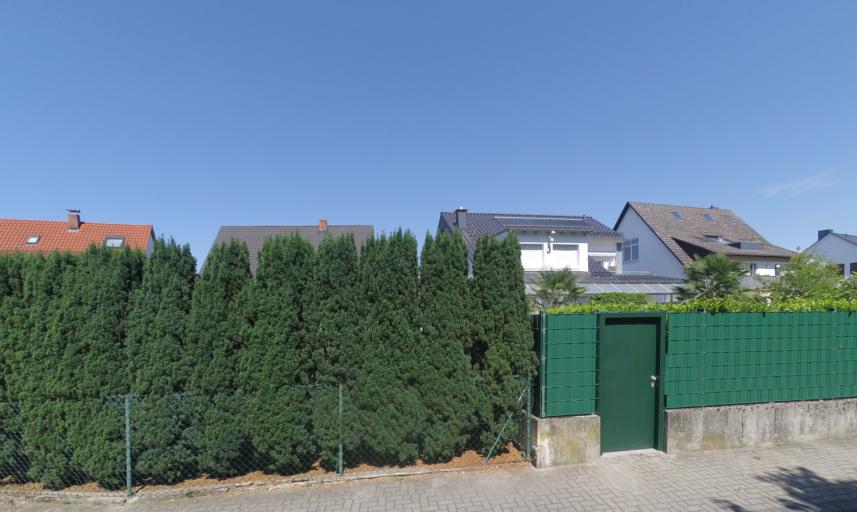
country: DE
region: Baden-Wuerttemberg
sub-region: Karlsruhe Region
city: Schwetzingen
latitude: 49.3893
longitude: 8.5627
